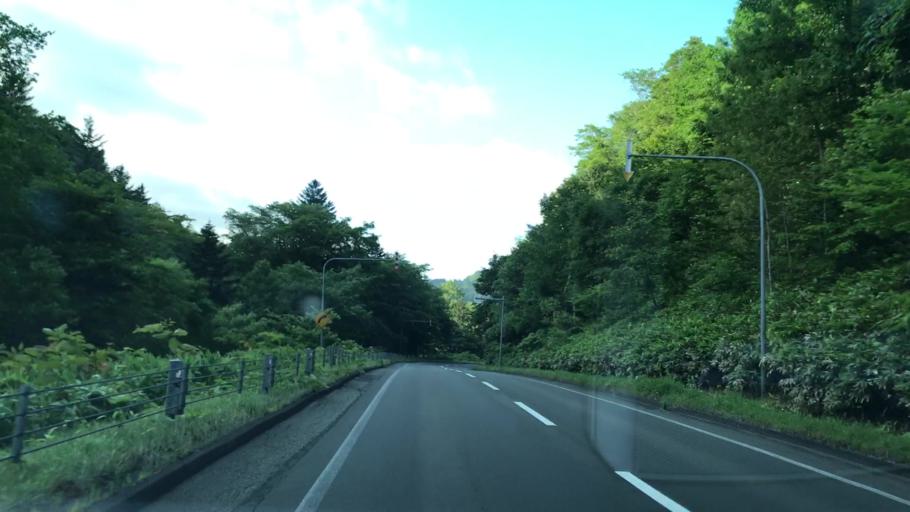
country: JP
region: Hokkaido
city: Iwamizawa
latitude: 42.8975
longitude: 142.1259
